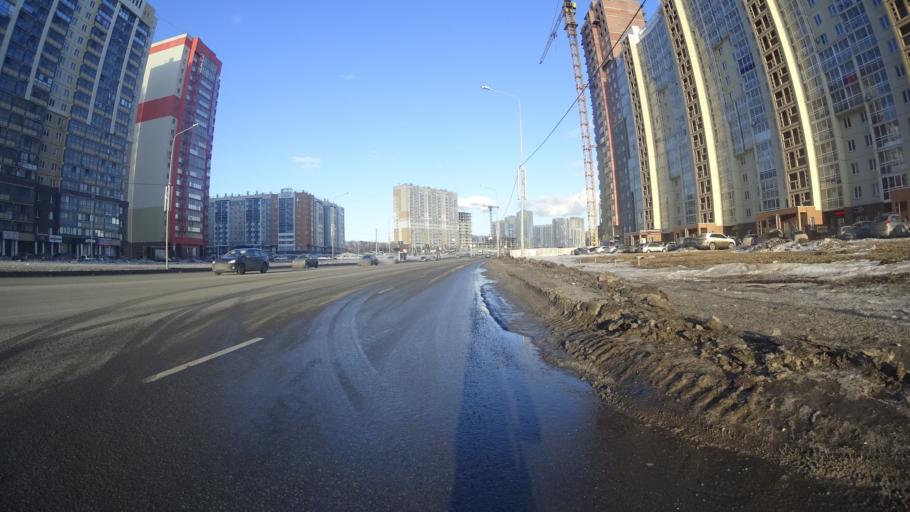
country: RU
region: Chelyabinsk
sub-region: Gorod Chelyabinsk
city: Chelyabinsk
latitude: 55.1726
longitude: 61.3145
